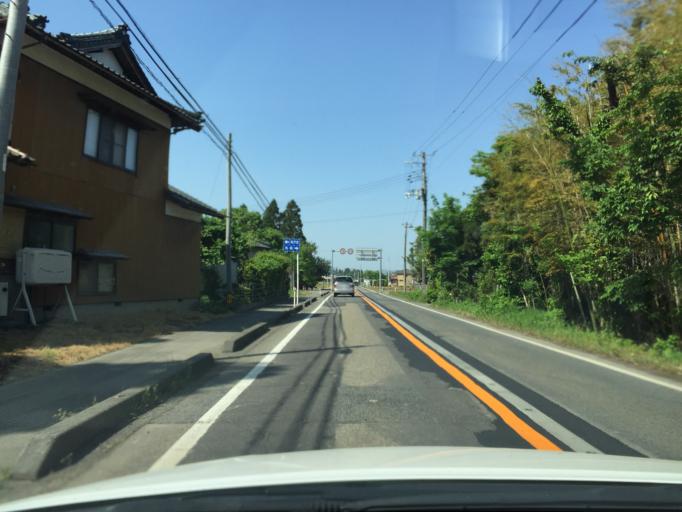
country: JP
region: Niigata
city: Muramatsu
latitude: 37.7046
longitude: 139.1975
